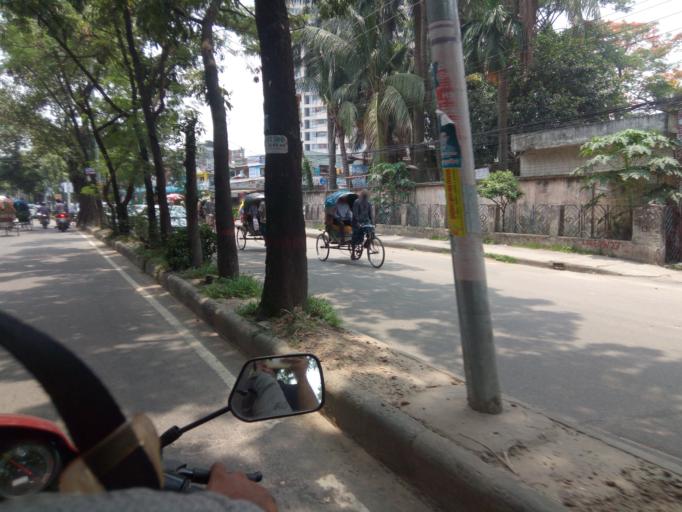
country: BD
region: Dhaka
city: Azimpur
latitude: 23.7341
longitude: 90.3877
